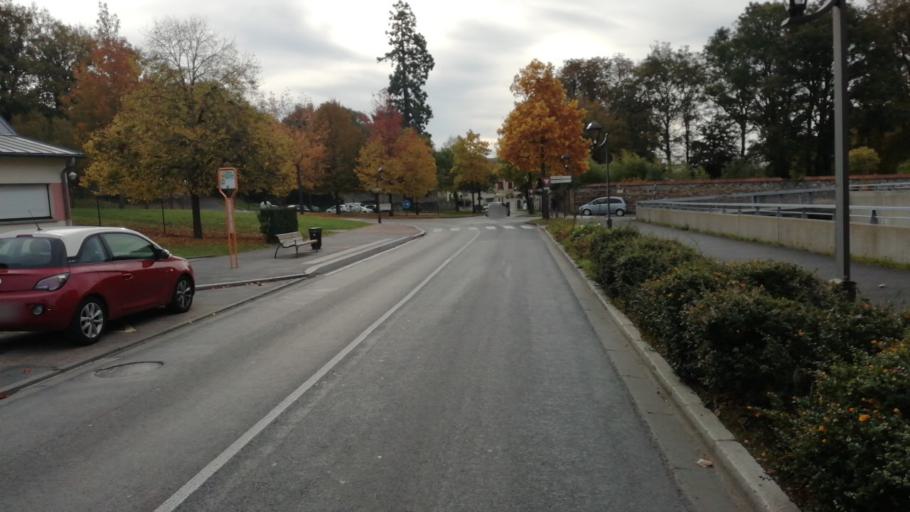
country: FR
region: Haute-Normandie
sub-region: Departement de la Seine-Maritime
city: Harfleur
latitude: 49.5101
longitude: 0.2006
